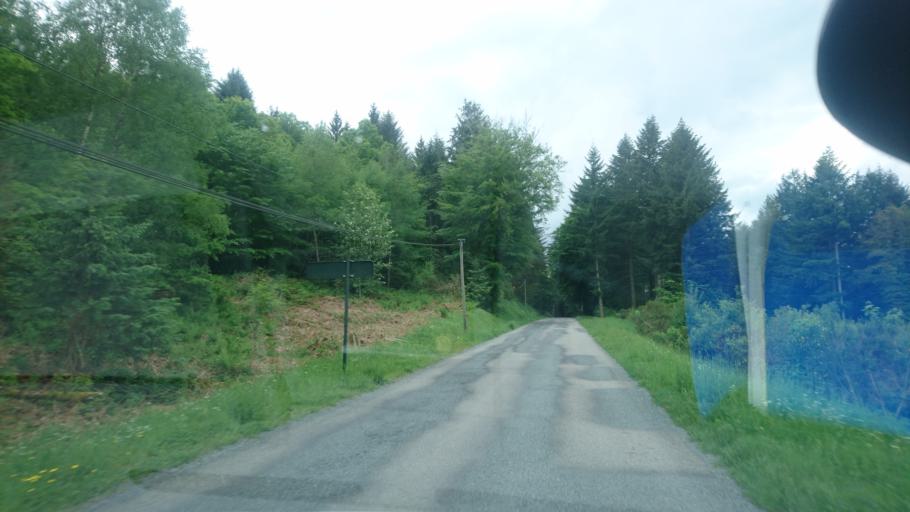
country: FR
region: Limousin
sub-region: Departement de la Haute-Vienne
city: Peyrat-le-Chateau
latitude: 45.8418
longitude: 1.9048
